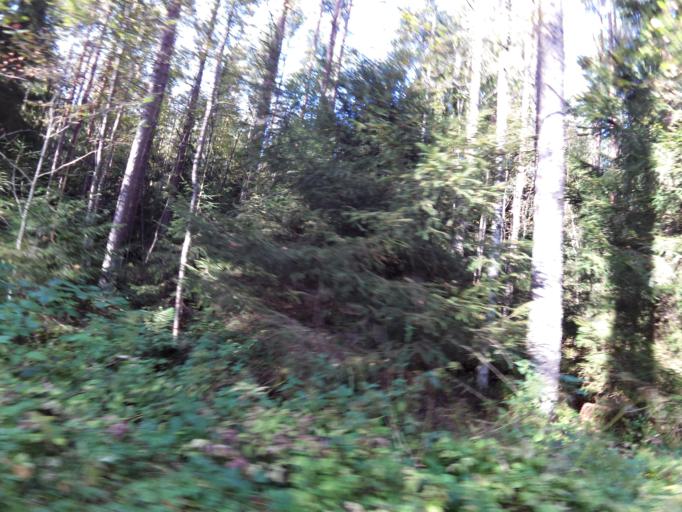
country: FI
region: Uusimaa
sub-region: Helsinki
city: Kauniainen
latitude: 60.1838
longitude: 24.6947
